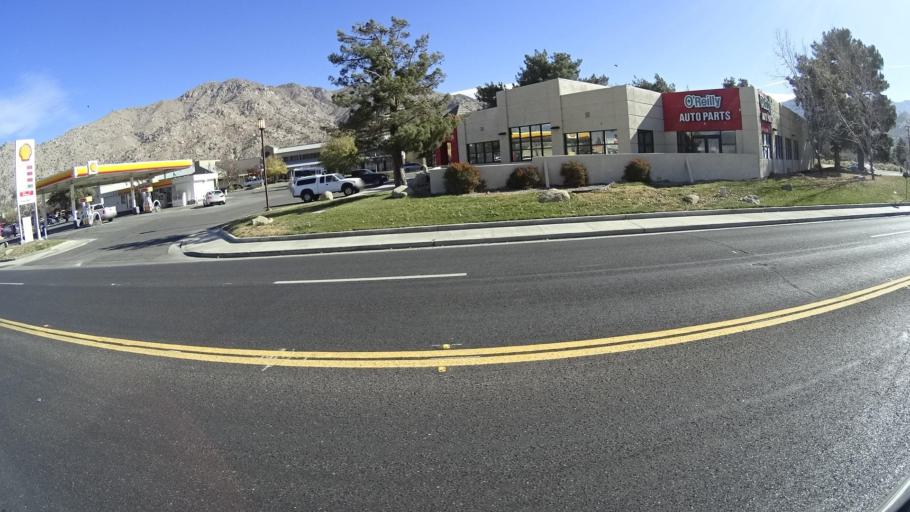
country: US
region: California
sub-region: Kern County
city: Lake Isabella
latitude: 35.6169
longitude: -118.4782
